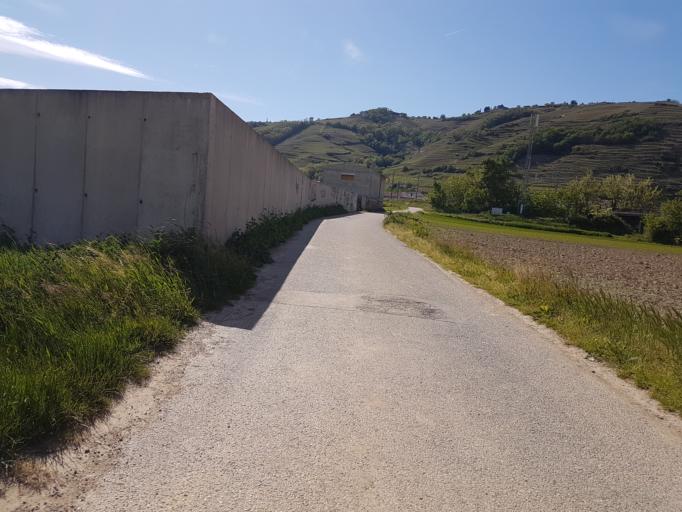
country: FR
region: Rhone-Alpes
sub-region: Departement du Rhone
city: Ampuis
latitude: 45.4833
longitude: 4.7963
